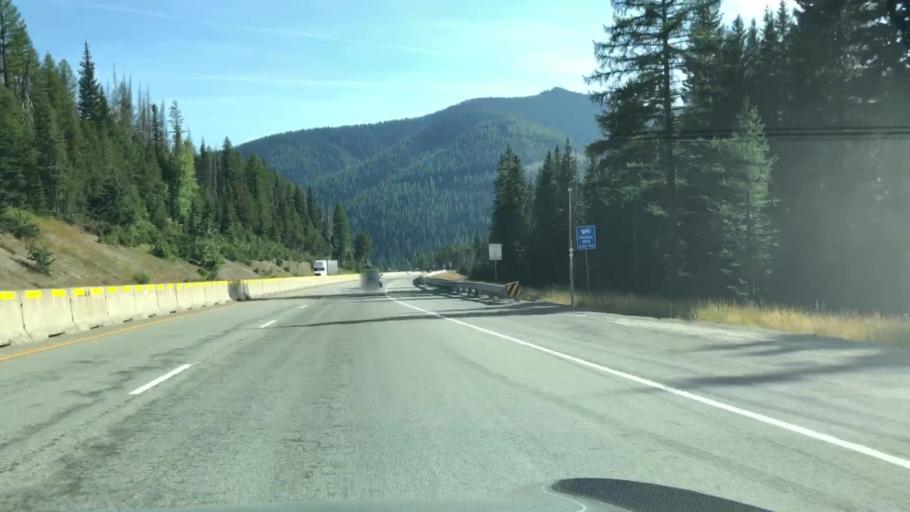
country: US
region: Idaho
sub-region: Shoshone County
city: Wallace
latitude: 47.4523
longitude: -115.6941
